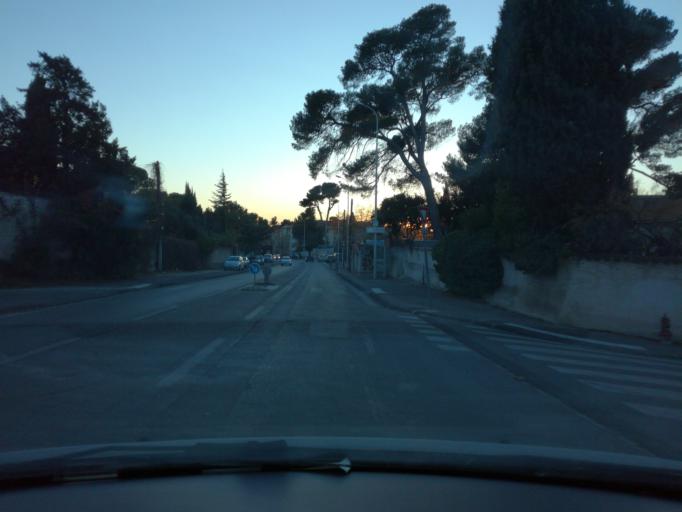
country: FR
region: Provence-Alpes-Cote d'Azur
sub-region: Departement des Bouches-du-Rhone
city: Allauch
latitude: 43.3147
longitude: 5.4672
